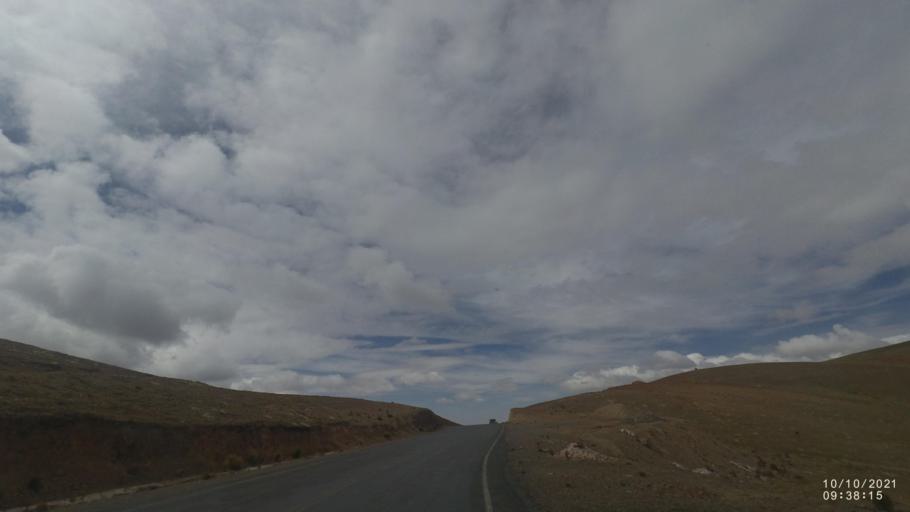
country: BO
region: La Paz
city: Quime
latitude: -17.1310
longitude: -67.3394
